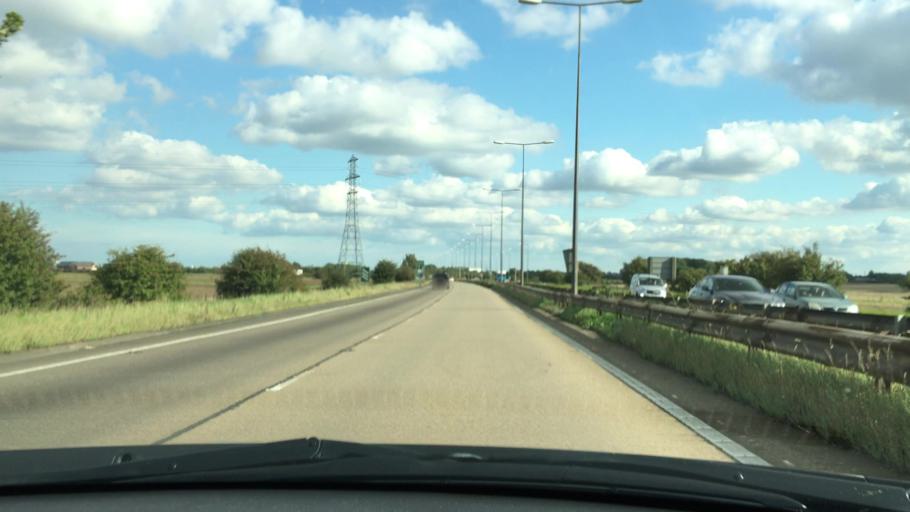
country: GB
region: England
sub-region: North East Lincolnshire
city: Healing
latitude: 53.5862
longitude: -0.1512
